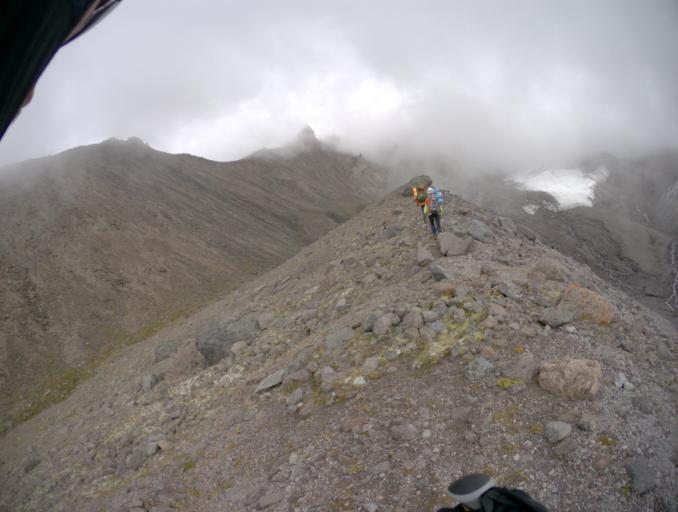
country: RU
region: Kabardino-Balkariya
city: Terskol
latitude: 43.3819
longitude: 42.3860
